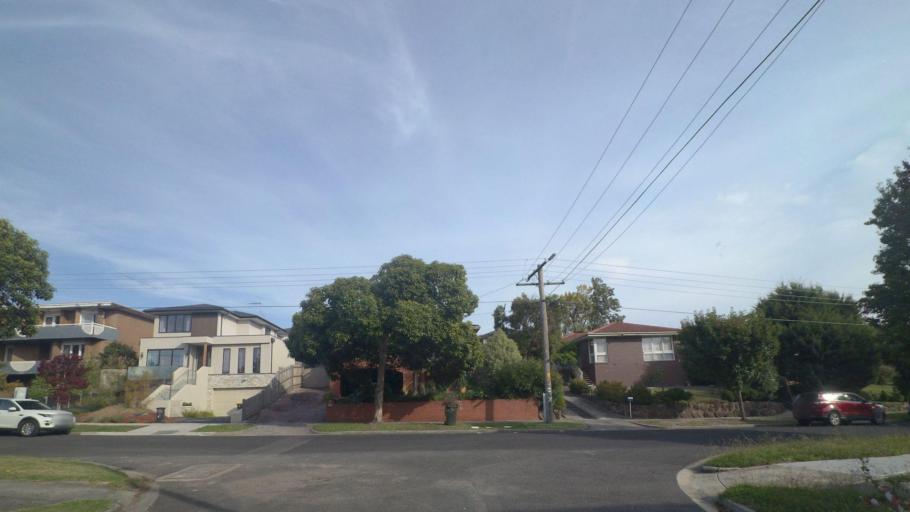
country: AU
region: Victoria
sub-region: Manningham
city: Doncaster East
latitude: -37.7802
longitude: 145.1554
